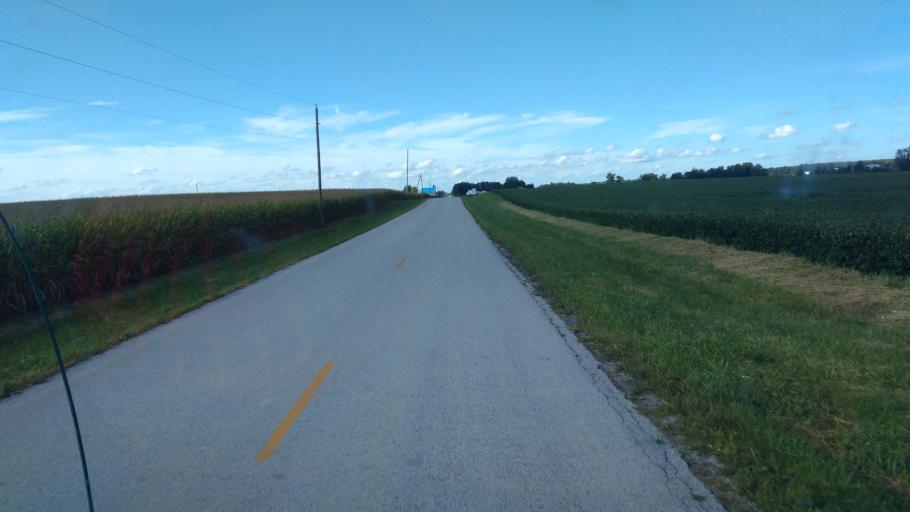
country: US
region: Ohio
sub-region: Hardin County
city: Kenton
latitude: 40.7375
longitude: -83.6908
